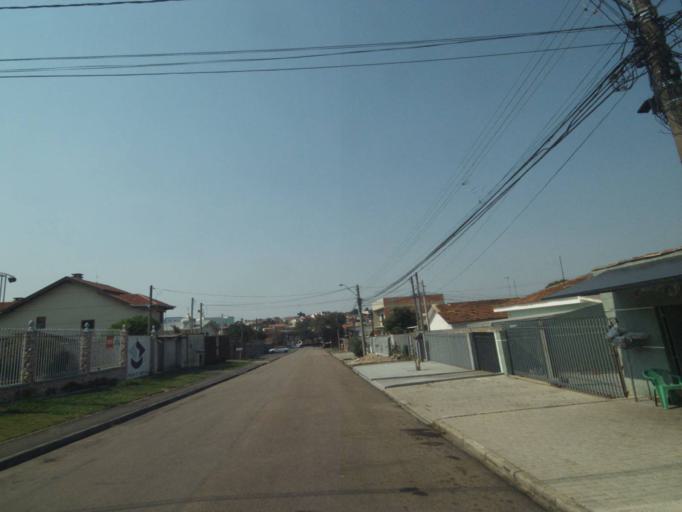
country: BR
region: Parana
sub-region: Sao Jose Dos Pinhais
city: Sao Jose dos Pinhais
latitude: -25.5122
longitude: -49.2764
